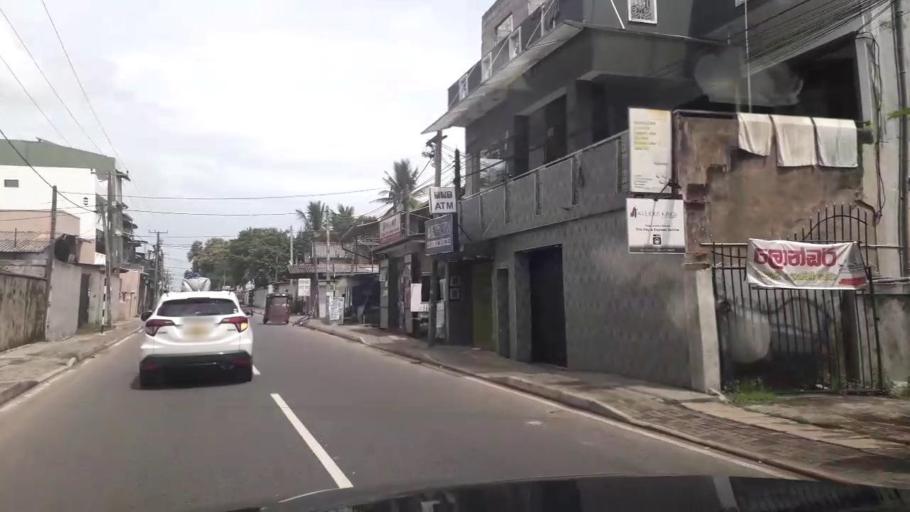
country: LK
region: Western
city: Moratuwa
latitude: 6.7520
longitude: 79.8999
